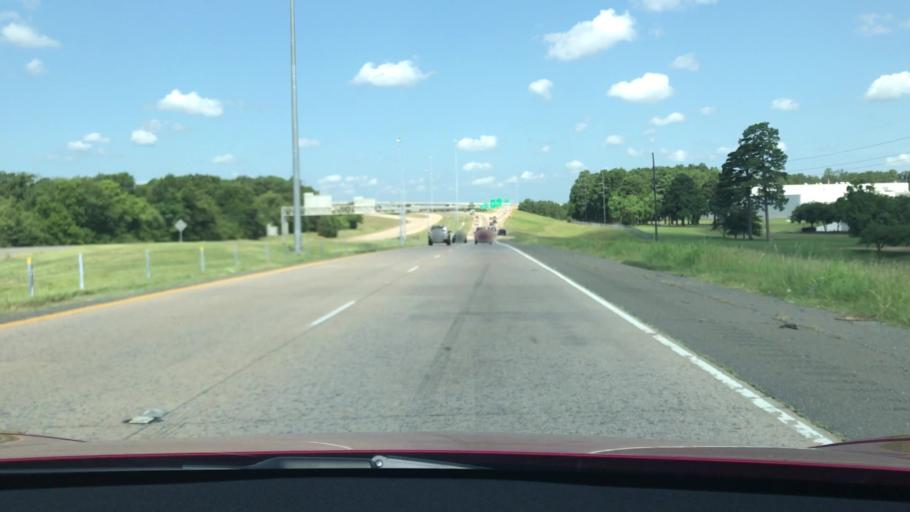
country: US
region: Louisiana
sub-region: Bossier Parish
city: Bossier City
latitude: 32.4164
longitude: -93.7382
